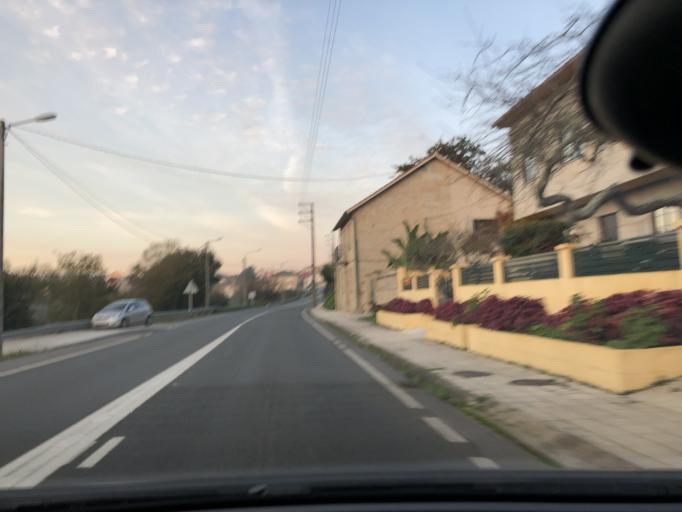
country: ES
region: Galicia
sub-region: Provincia de Pontevedra
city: Marin
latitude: 42.3821
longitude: -8.7156
